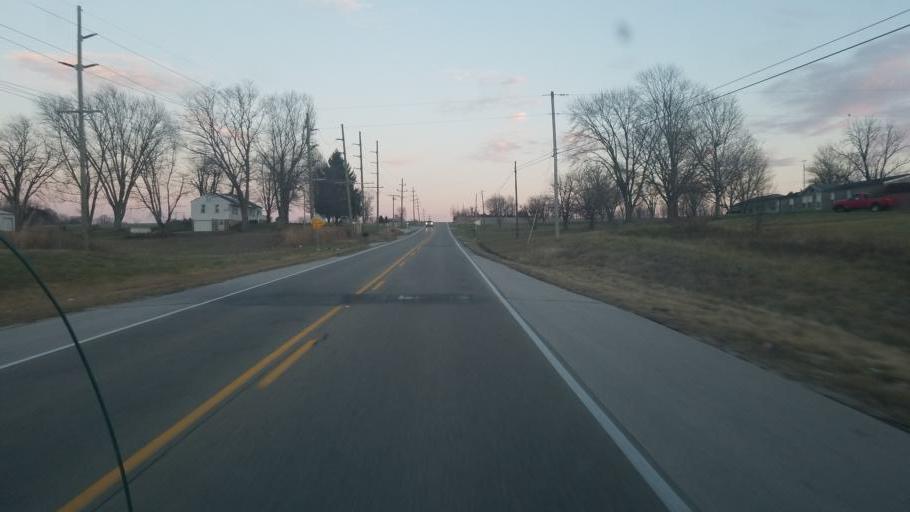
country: US
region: Indiana
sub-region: Lawrence County
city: Bedford
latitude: 38.8751
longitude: -86.3771
